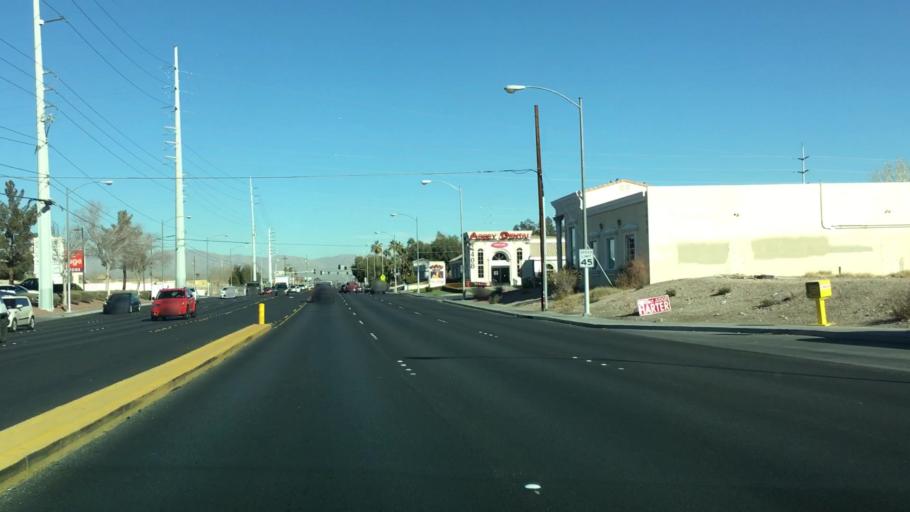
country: US
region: Nevada
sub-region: Clark County
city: Winchester
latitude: 36.1079
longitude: -115.1191
